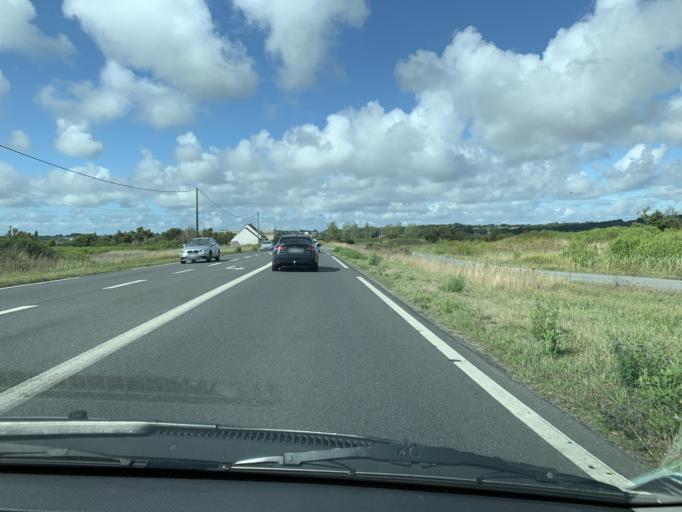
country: FR
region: Pays de la Loire
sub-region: Departement de la Loire-Atlantique
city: Guerande
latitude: 47.3028
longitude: -2.4309
